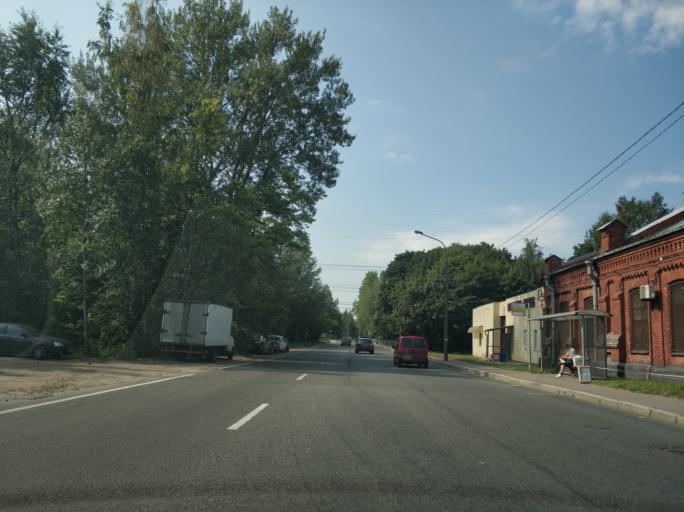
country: RU
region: St.-Petersburg
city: Krasnogvargeisky
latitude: 59.9789
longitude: 30.5021
